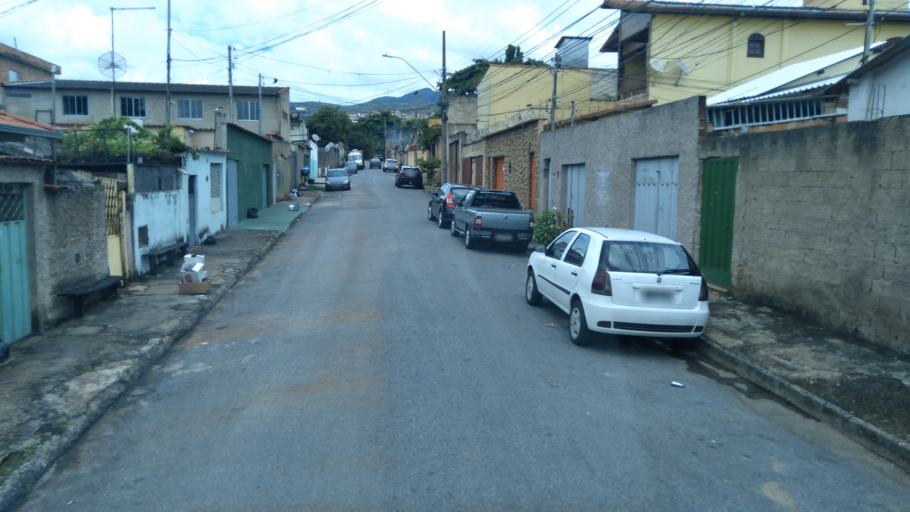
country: BR
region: Minas Gerais
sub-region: Belo Horizonte
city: Belo Horizonte
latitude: -19.9085
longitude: -43.8956
